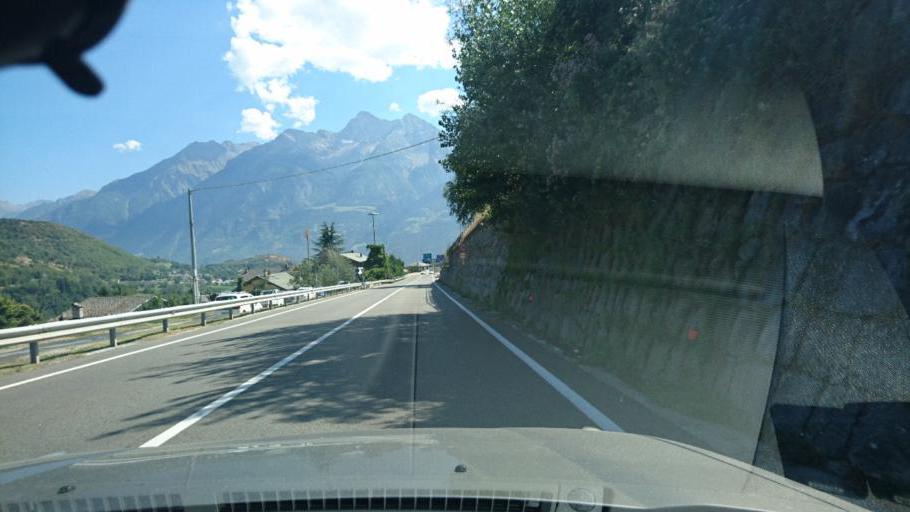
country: IT
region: Aosta Valley
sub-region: Valle d'Aosta
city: La Cretaz-Roisan
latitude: 45.7683
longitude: 7.3103
